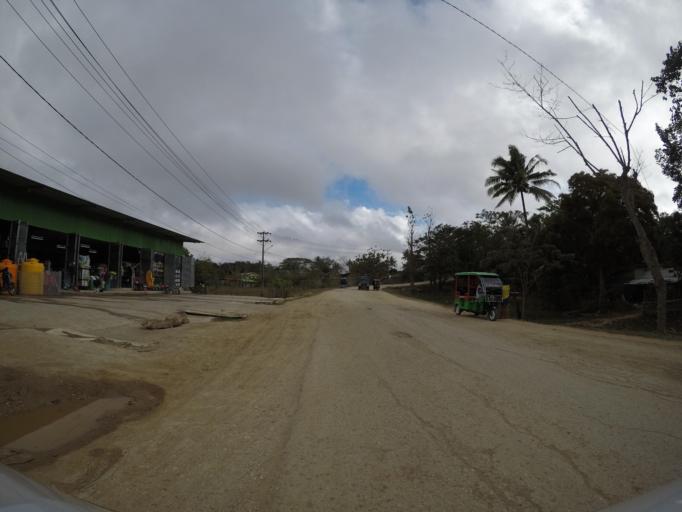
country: TL
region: Lautem
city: Lospalos
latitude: -8.5108
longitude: 126.9865
